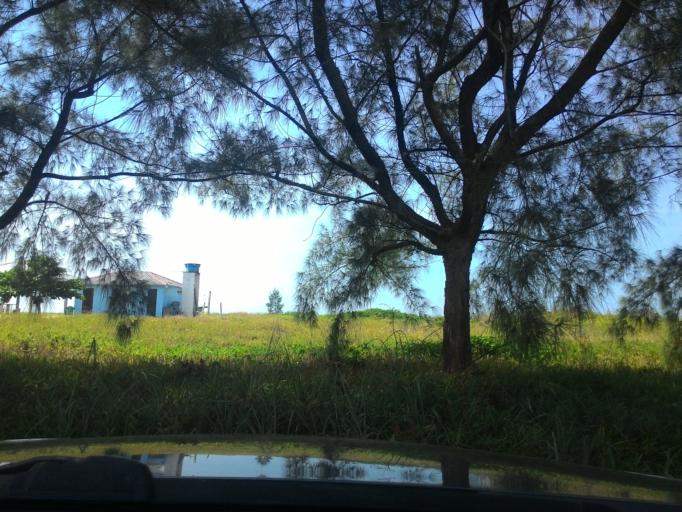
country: BR
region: Sao Paulo
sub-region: Iguape
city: Iguape
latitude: -24.8526
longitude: -47.6979
